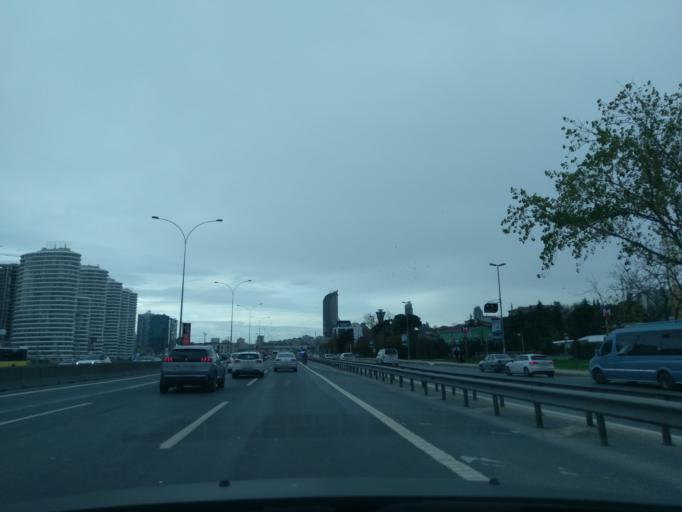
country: TR
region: Istanbul
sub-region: Atasehir
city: Atasehir
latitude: 40.9935
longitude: 29.0711
